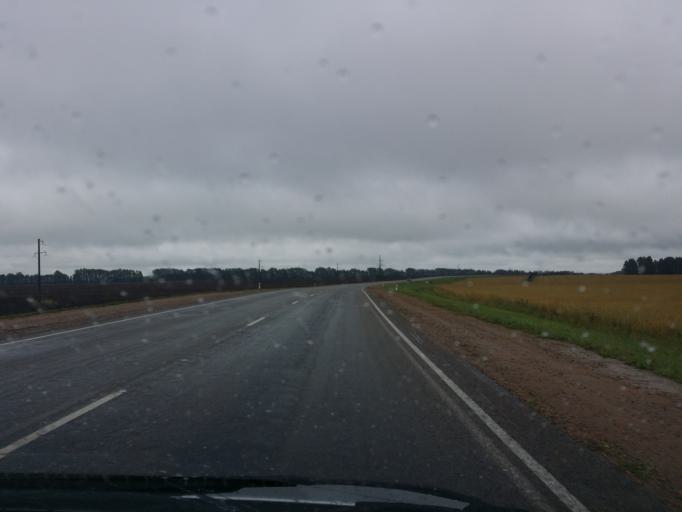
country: RU
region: Altai Krai
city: Nalobikha
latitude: 53.2462
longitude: 84.5838
